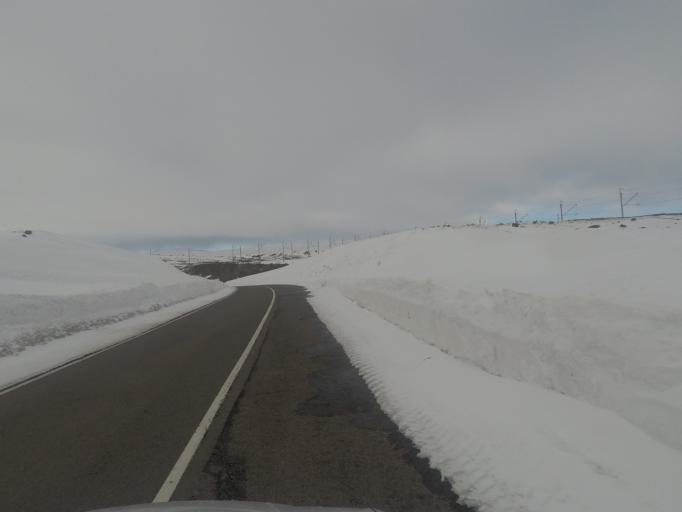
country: GE
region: Kvemo Kartli
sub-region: Tsalka
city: Tsalka
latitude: 41.4407
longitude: 43.8483
